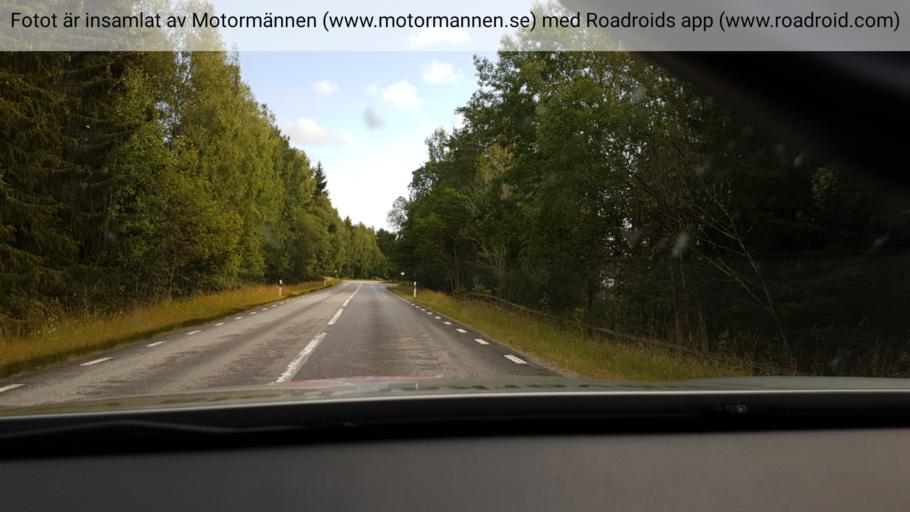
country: SE
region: Stockholm
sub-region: Norrtalje Kommun
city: Norrtalje
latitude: 59.5662
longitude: 18.6138
